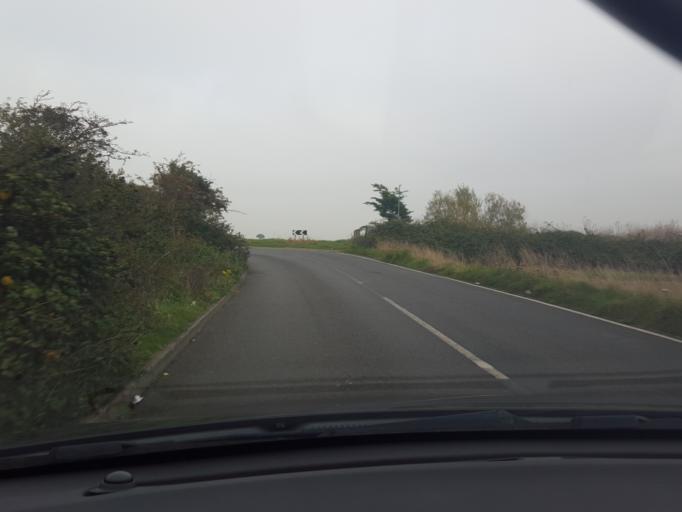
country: GB
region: England
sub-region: Essex
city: Saint Osyth
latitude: 51.7814
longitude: 1.0885
